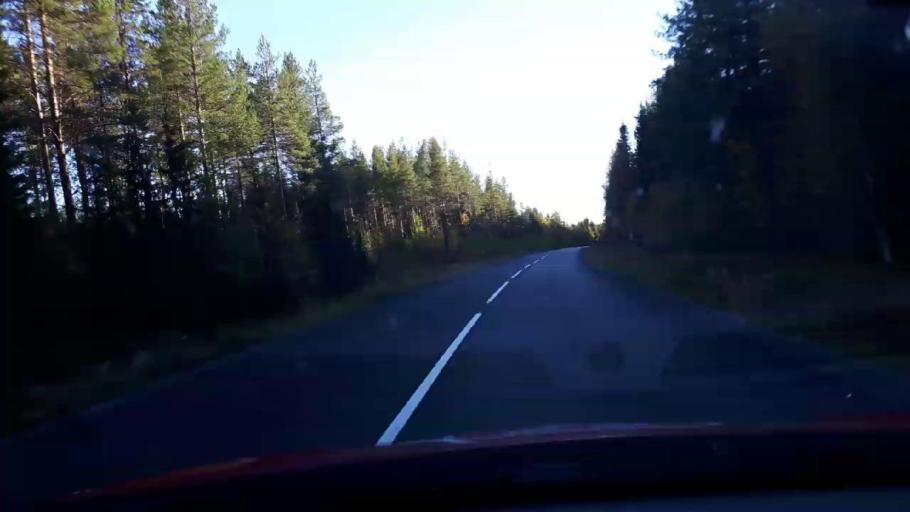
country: SE
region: Jaemtland
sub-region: OEstersunds Kommun
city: Lit
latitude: 63.4692
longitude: 14.8760
